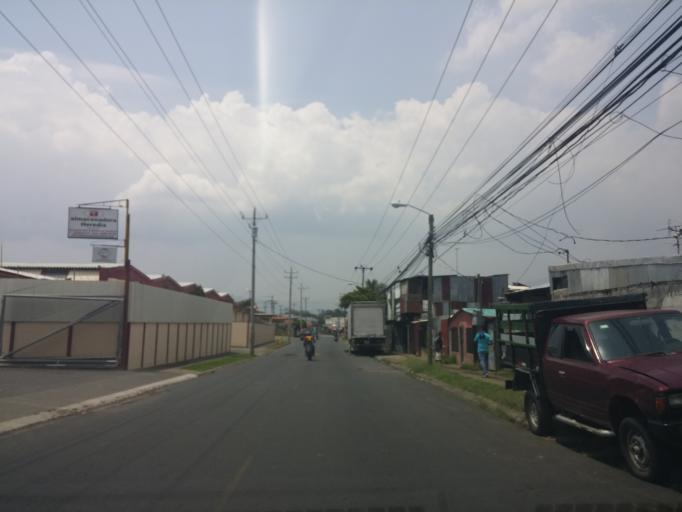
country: CR
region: Heredia
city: San Francisco
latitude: 9.9802
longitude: -84.1143
